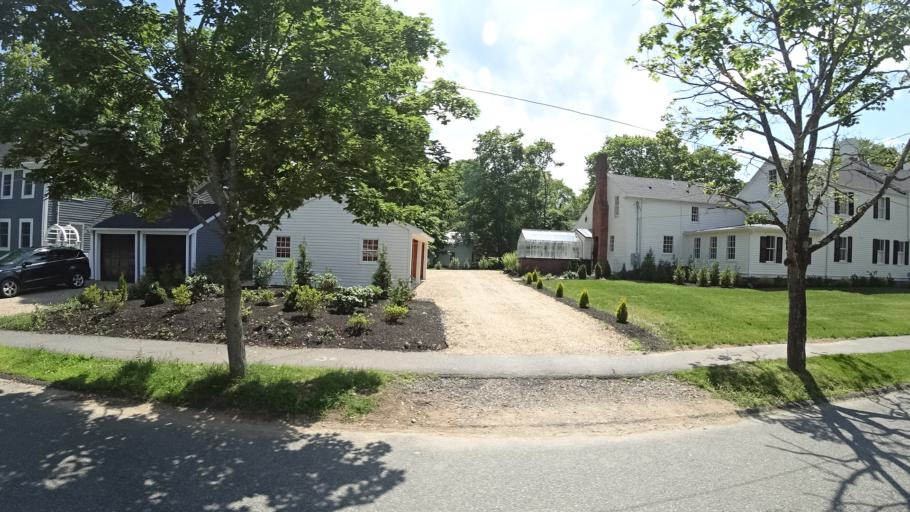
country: US
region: Massachusetts
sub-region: Norfolk County
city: Dedham
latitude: 42.2505
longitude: -71.1866
